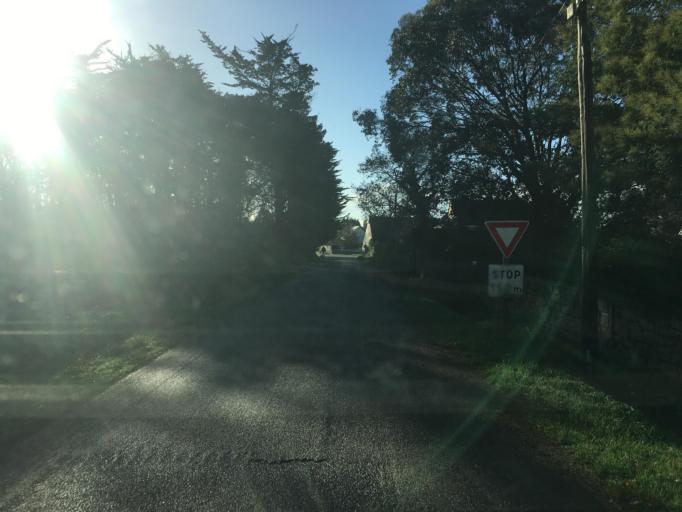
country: FR
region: Brittany
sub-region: Departement du Morbihan
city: Sene
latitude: 47.5749
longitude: -2.7142
